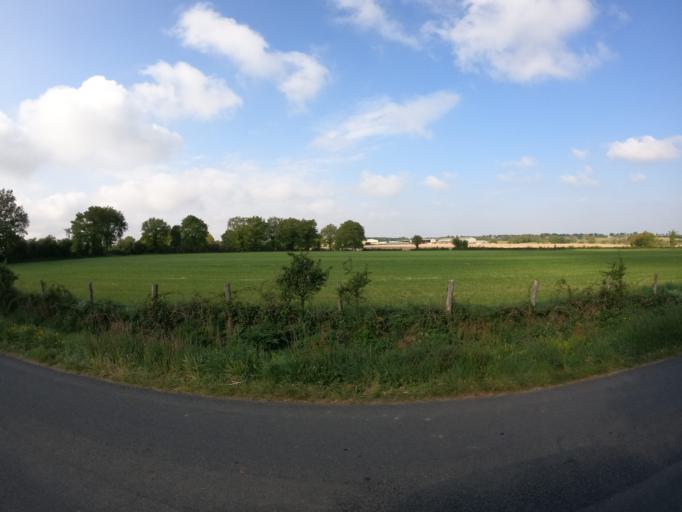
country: FR
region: Pays de la Loire
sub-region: Departement de Maine-et-Loire
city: La Romagne
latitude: 47.0673
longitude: -1.0452
